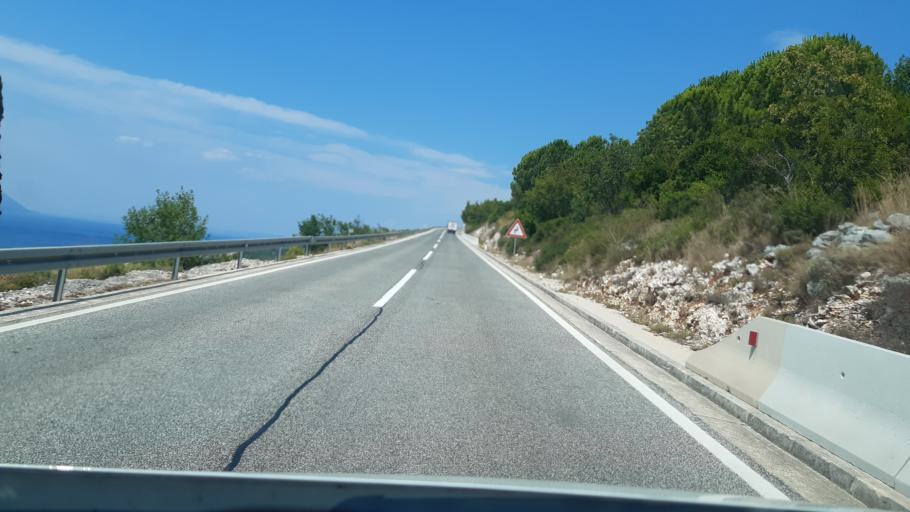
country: HR
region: Dubrovacko-Neretvanska
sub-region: Grad Dubrovnik
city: Opuzen
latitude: 42.9622
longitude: 17.5204
